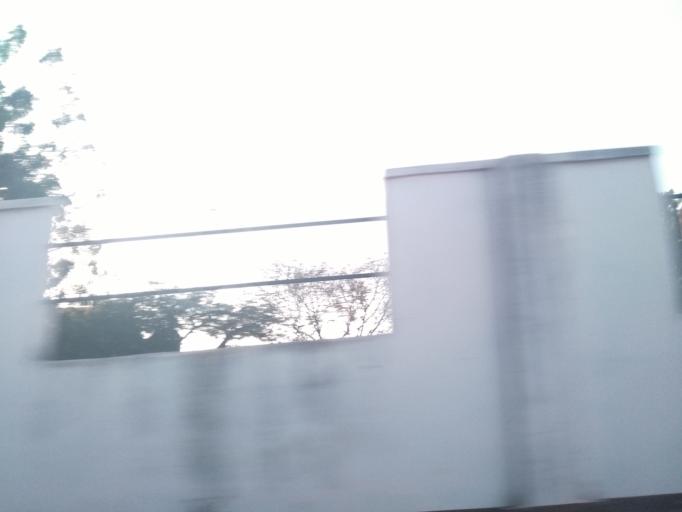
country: TZ
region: Dar es Salaam
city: Magomeni
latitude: -6.7804
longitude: 39.2827
